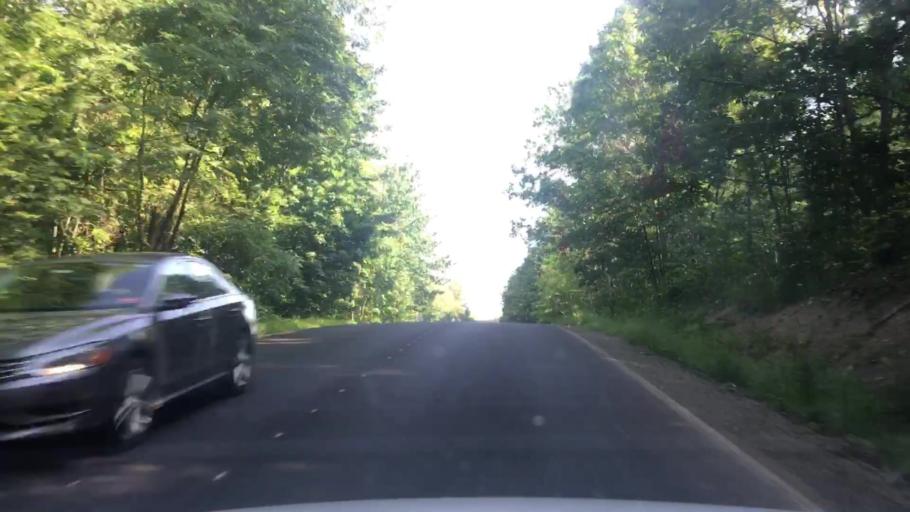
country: US
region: Maine
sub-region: Kennebec County
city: Waterville
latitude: 44.5739
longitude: -69.6580
